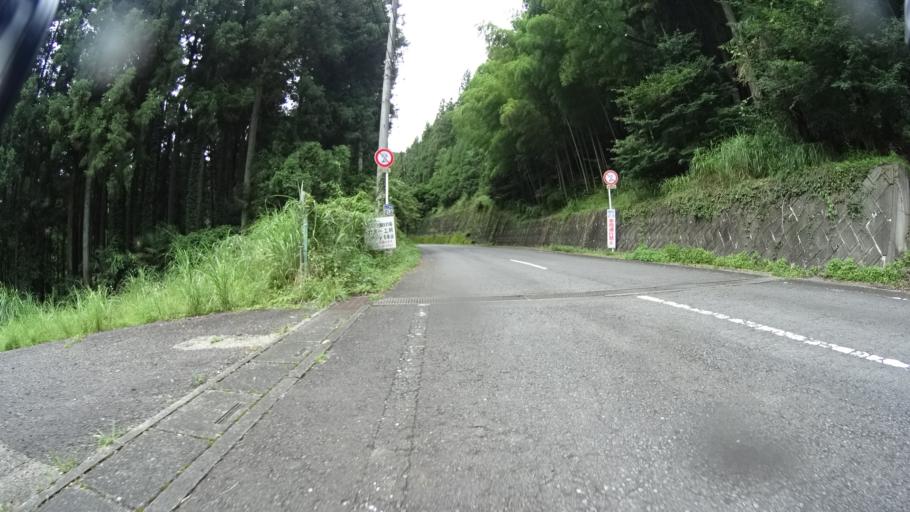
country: JP
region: Tokyo
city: Ome
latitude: 35.8731
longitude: 139.1821
